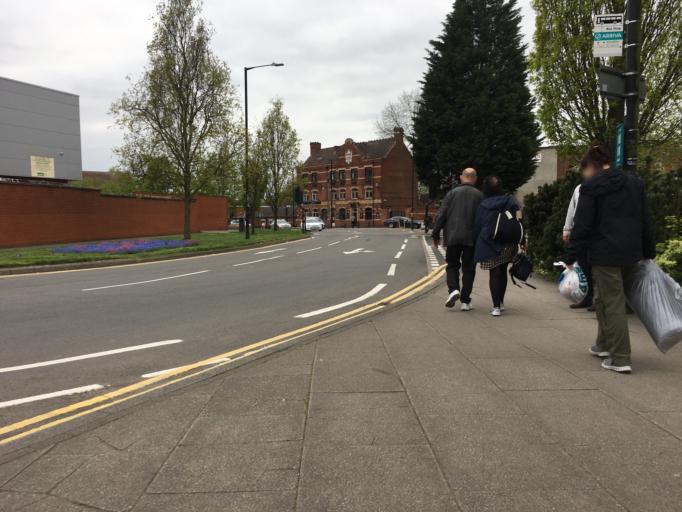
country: GB
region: England
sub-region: Warwickshire
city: Nuneaton
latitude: 52.5257
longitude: -1.4643
